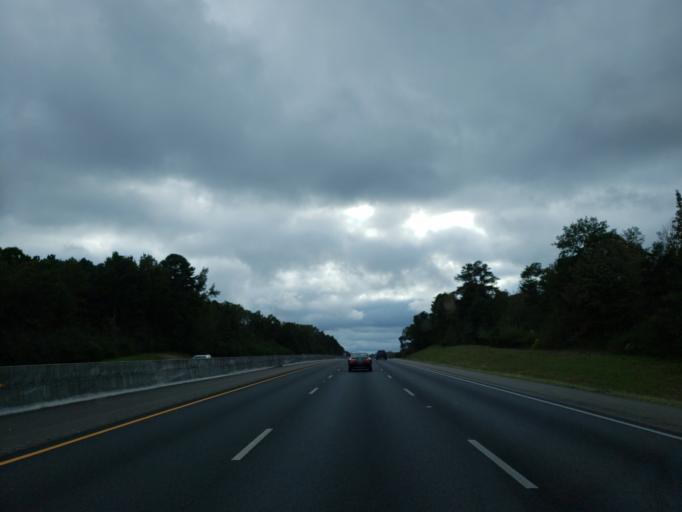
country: US
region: Alabama
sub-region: Bibb County
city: Woodstock
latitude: 33.2380
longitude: -87.1562
